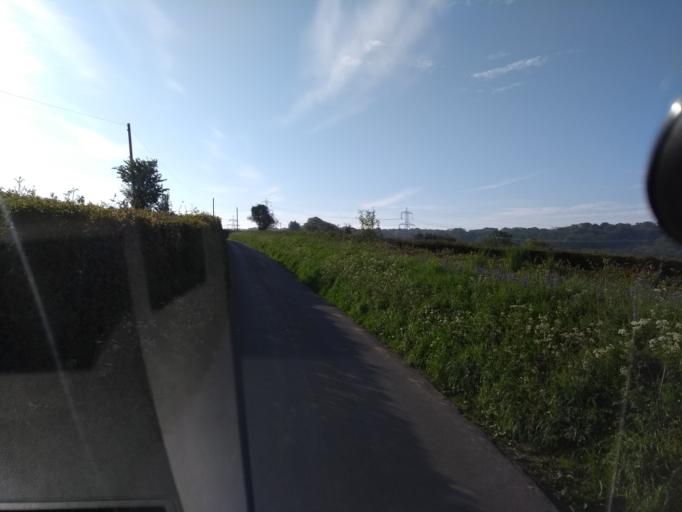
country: GB
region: England
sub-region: Devon
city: Axminster
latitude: 50.7916
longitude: -2.9409
